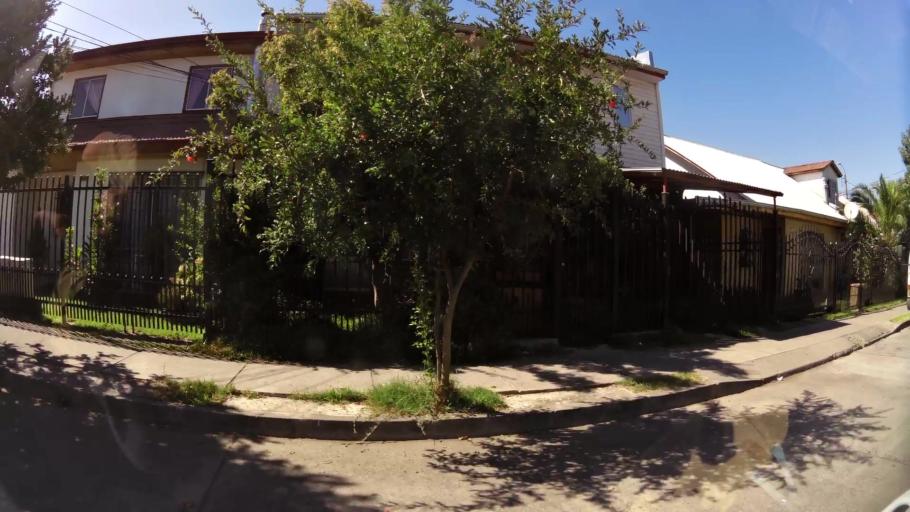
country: CL
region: Maule
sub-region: Provincia de Curico
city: Curico
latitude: -34.9718
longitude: -71.2582
